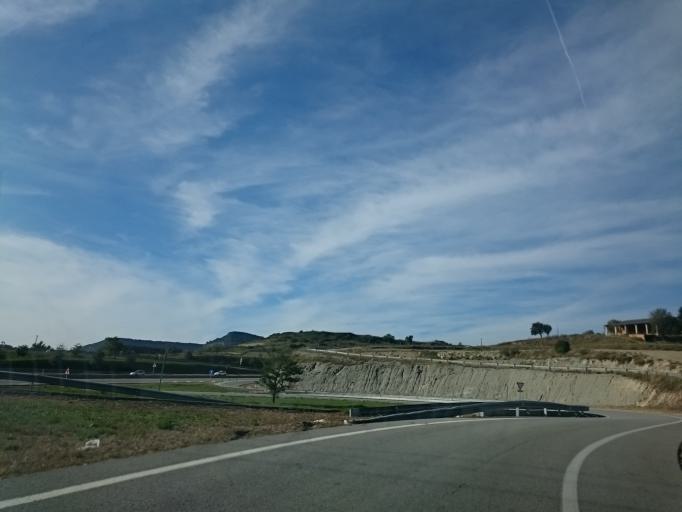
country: ES
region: Catalonia
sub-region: Provincia de Barcelona
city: Vic
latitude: 41.9275
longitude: 2.2323
